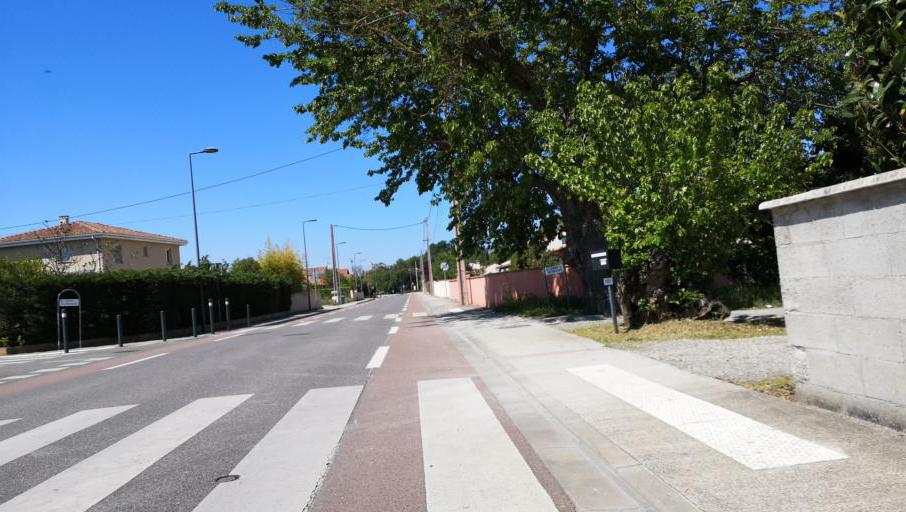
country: FR
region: Midi-Pyrenees
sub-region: Departement de la Haute-Garonne
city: Blagnac
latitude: 43.6494
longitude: 1.3864
